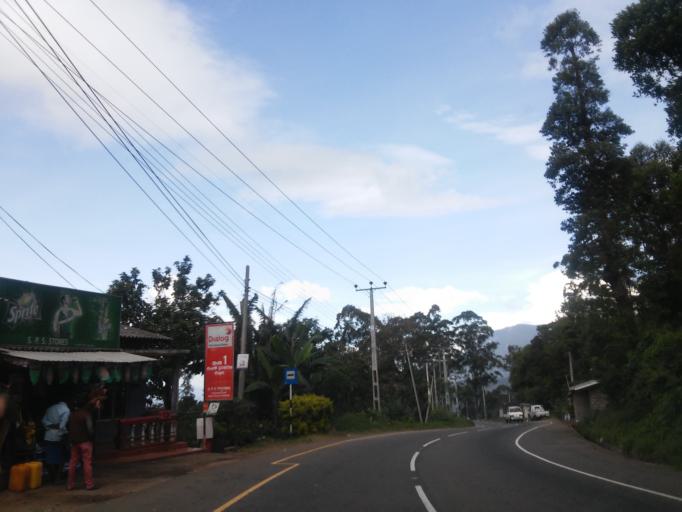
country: LK
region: Uva
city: Haputale
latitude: 6.7629
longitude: 80.9246
